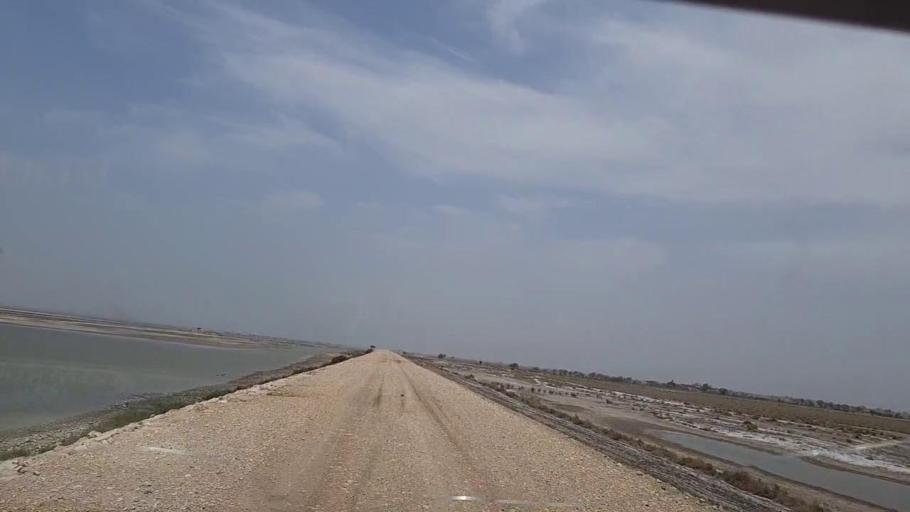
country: PK
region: Sindh
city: Sehwan
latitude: 26.4150
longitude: 67.7627
